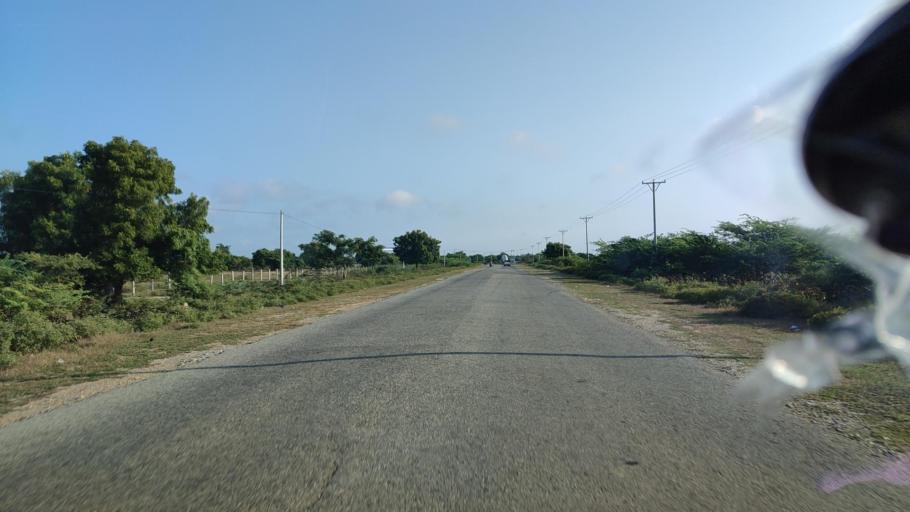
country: MM
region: Mandalay
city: Yamethin
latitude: 20.6192
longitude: 96.0786
